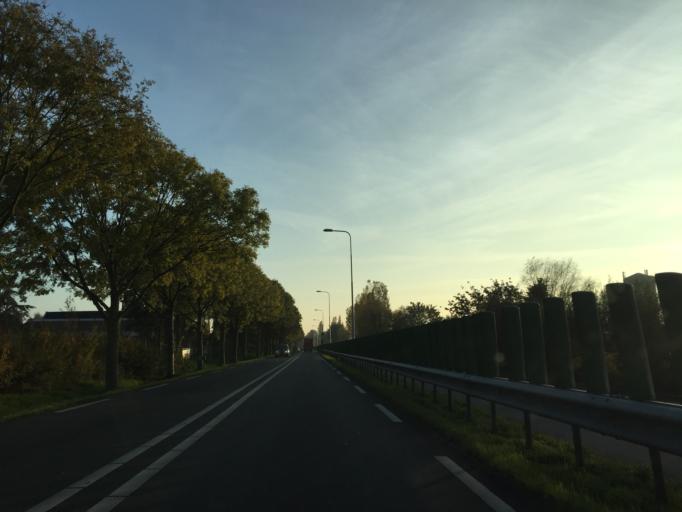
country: NL
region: South Holland
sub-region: Gemeente Lansingerland
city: Bleiswijk
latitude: 52.0133
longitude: 4.5267
